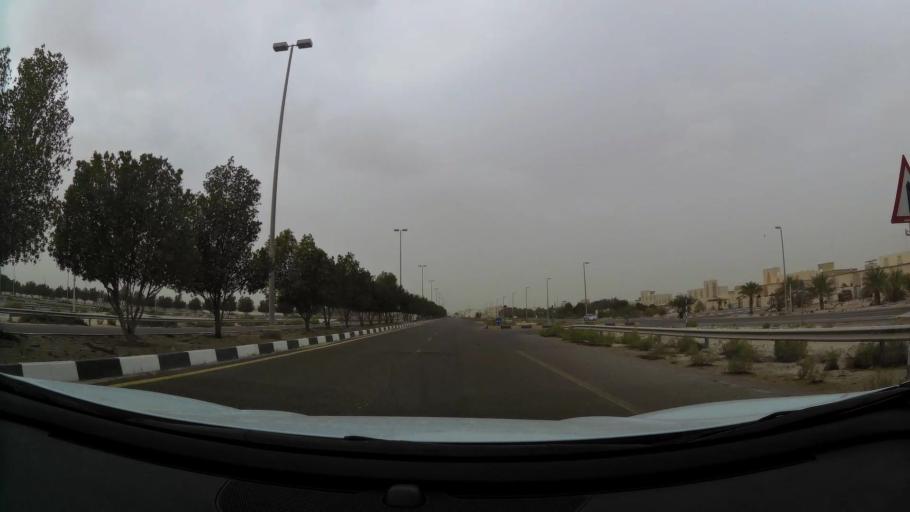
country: AE
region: Abu Dhabi
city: Abu Dhabi
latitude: 24.3905
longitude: 54.7088
